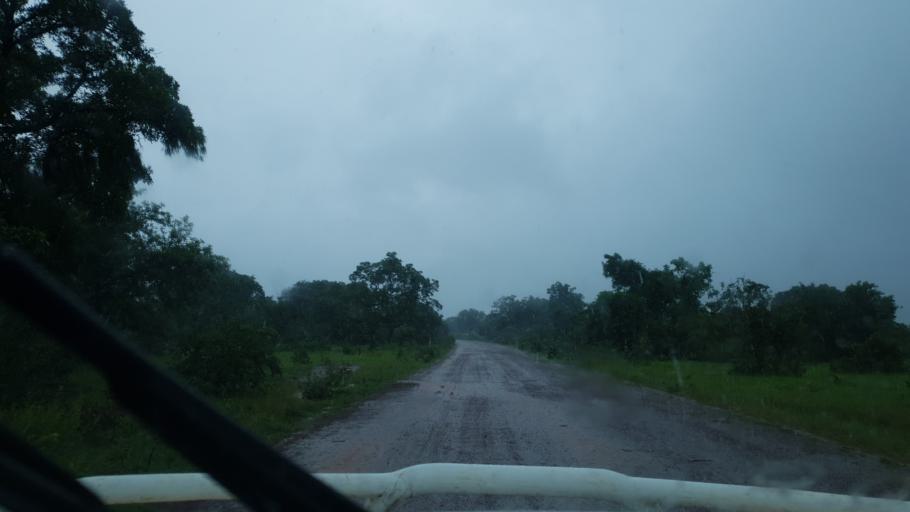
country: ML
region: Sikasso
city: Kolondieba
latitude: 11.6123
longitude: -6.6759
